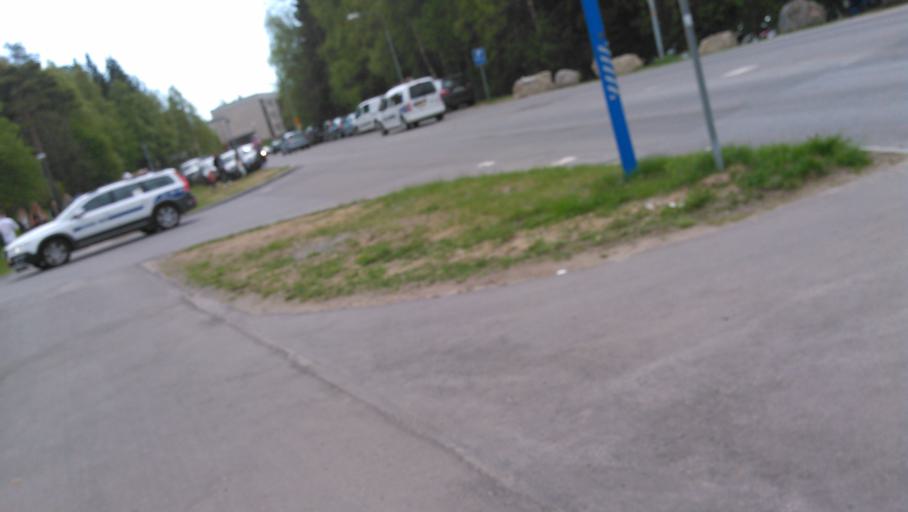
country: SE
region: Vaesterbotten
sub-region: Umea Kommun
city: Ersmark
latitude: 63.8343
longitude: 20.3188
